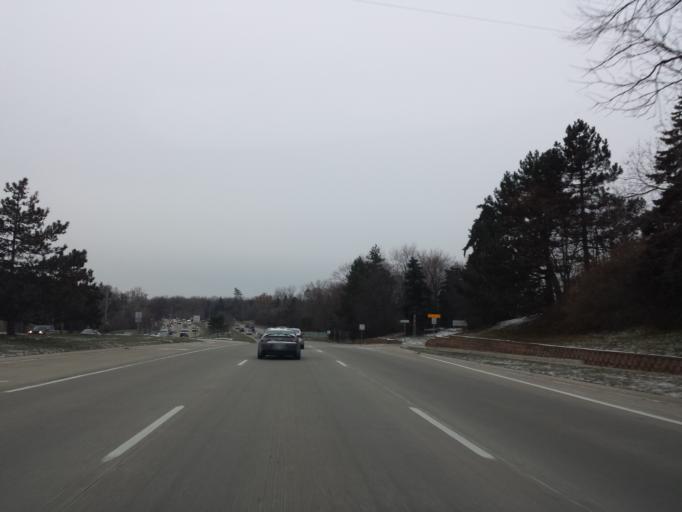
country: US
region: Michigan
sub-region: Oakland County
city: Bloomfield Hills
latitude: 42.5633
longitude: -83.2842
